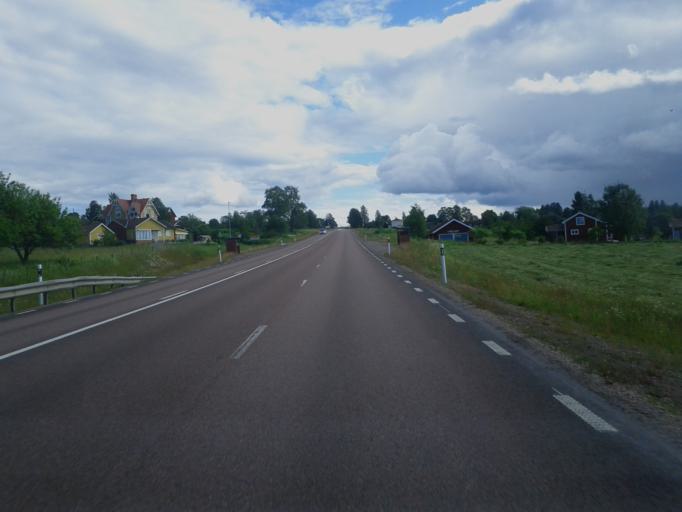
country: SE
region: Dalarna
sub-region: Rattviks Kommun
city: Raettvik
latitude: 60.8485
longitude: 15.1159
